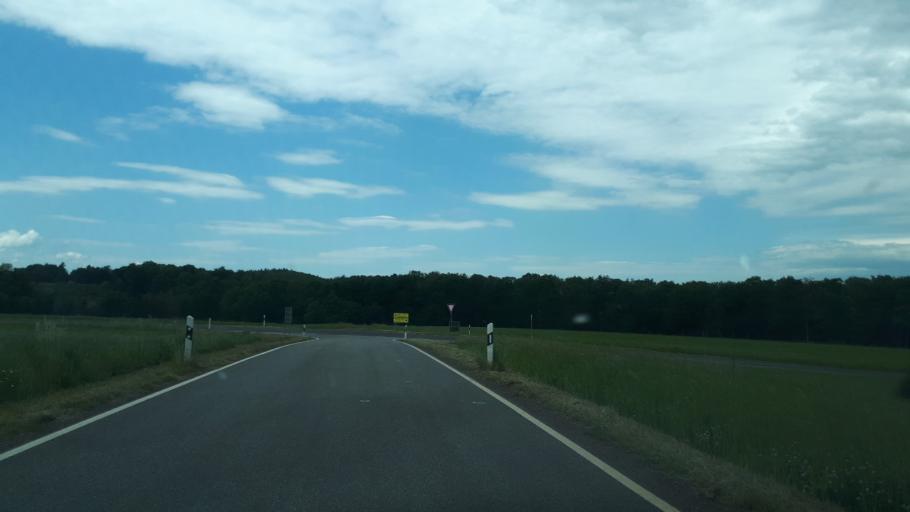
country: DE
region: Rheinland-Pfalz
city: Wagenhausen
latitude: 50.1340
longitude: 6.9737
